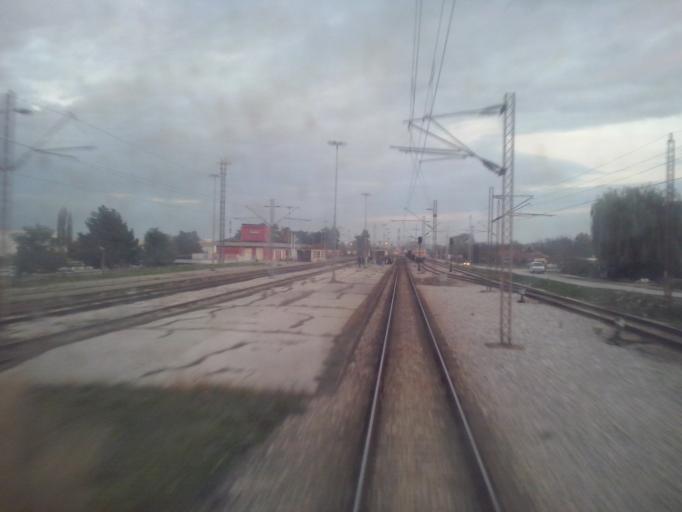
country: RS
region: Central Serbia
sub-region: Kolubarski Okrug
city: Valjevo
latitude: 44.2703
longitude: 19.9052
